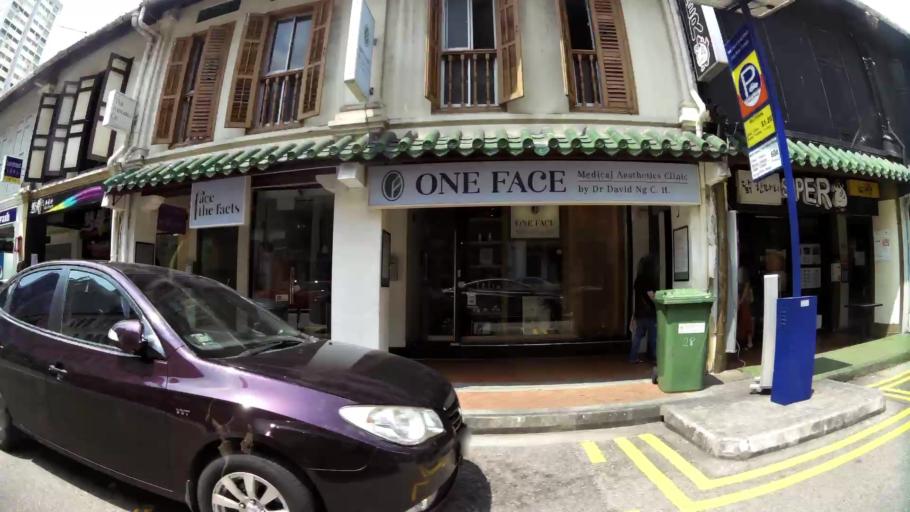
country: SG
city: Singapore
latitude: 1.2781
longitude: 103.8437
